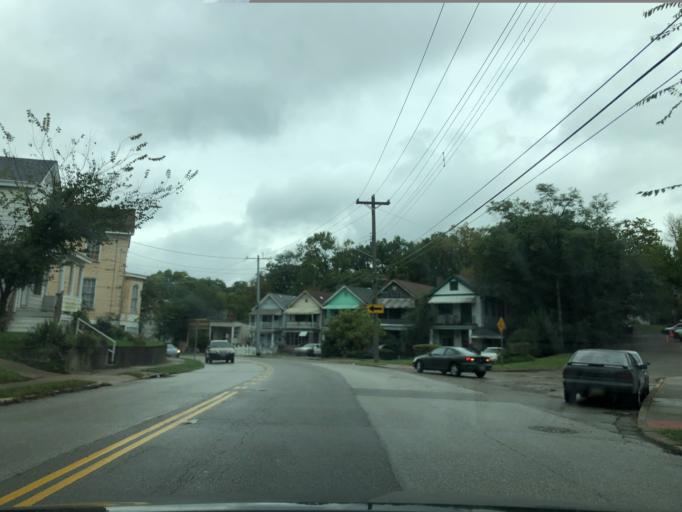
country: US
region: Ohio
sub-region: Hamilton County
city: Saint Bernard
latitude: 39.1481
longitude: -84.5086
